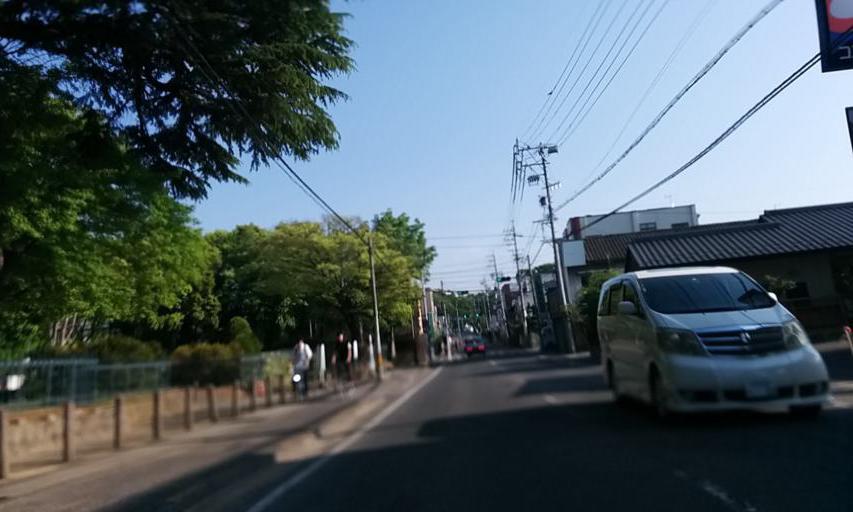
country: JP
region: Nagano
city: Matsumoto
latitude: 36.2303
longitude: 137.9817
